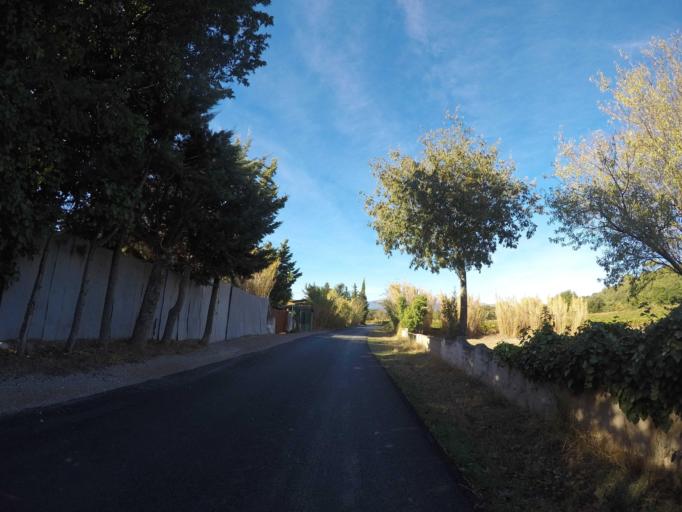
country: FR
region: Languedoc-Roussillon
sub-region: Departement des Pyrenees-Orientales
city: Llupia
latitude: 42.6052
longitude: 2.7711
